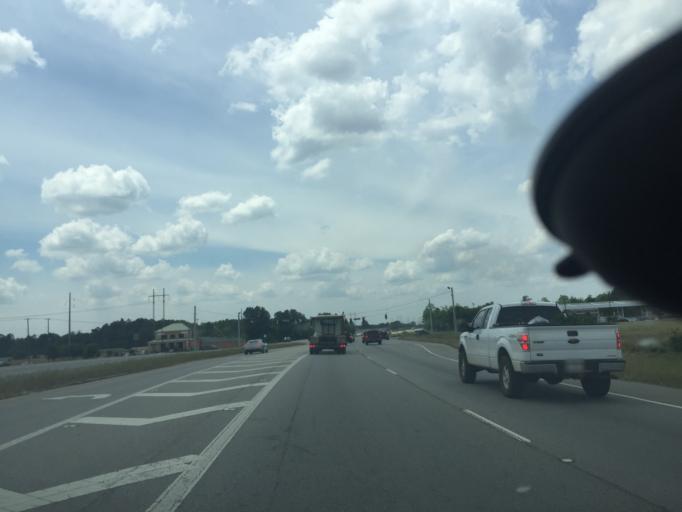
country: US
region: Georgia
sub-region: Bulloch County
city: Statesboro
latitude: 32.4060
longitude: -81.7680
